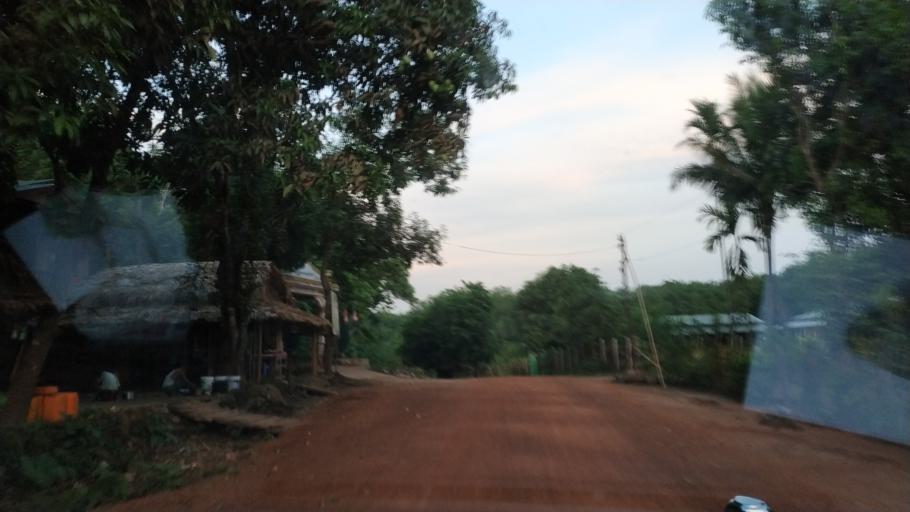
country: MM
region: Mon
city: Kyaikto
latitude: 17.4225
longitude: 97.0492
